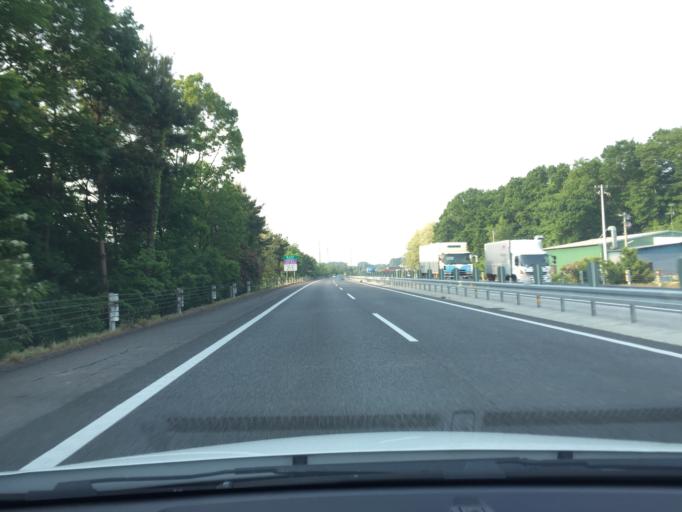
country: JP
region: Fukushima
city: Sukagawa
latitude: 37.2474
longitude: 140.3310
